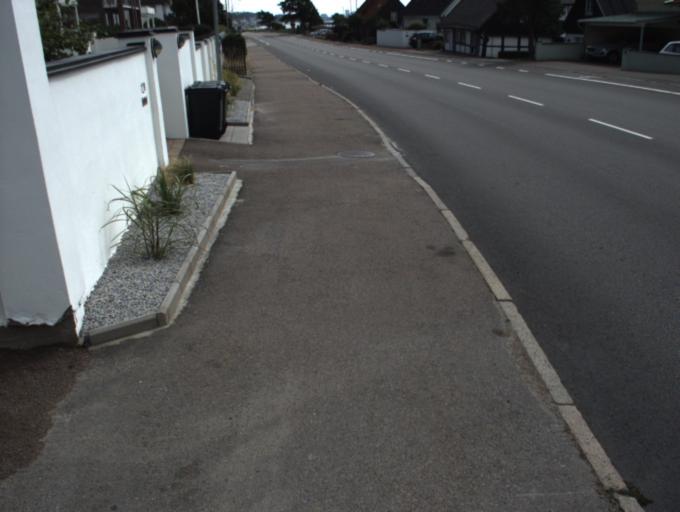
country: SE
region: Skane
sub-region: Helsingborg
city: Helsingborg
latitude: 56.0722
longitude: 12.6692
